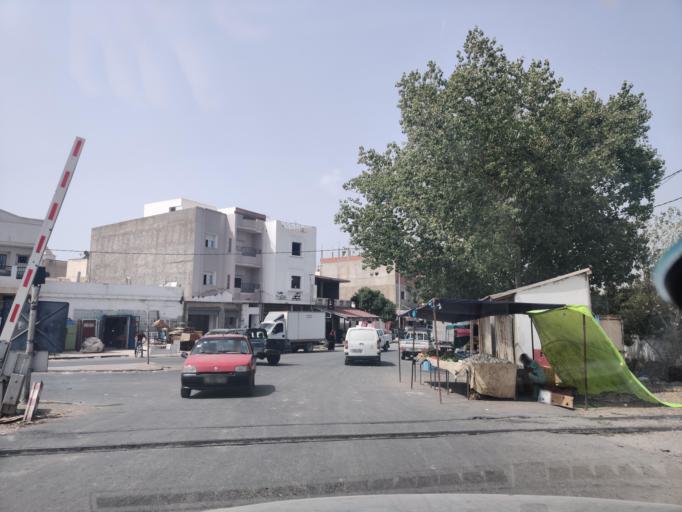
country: TN
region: Nabul
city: Bu `Urqub
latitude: 36.5995
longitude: 10.4951
